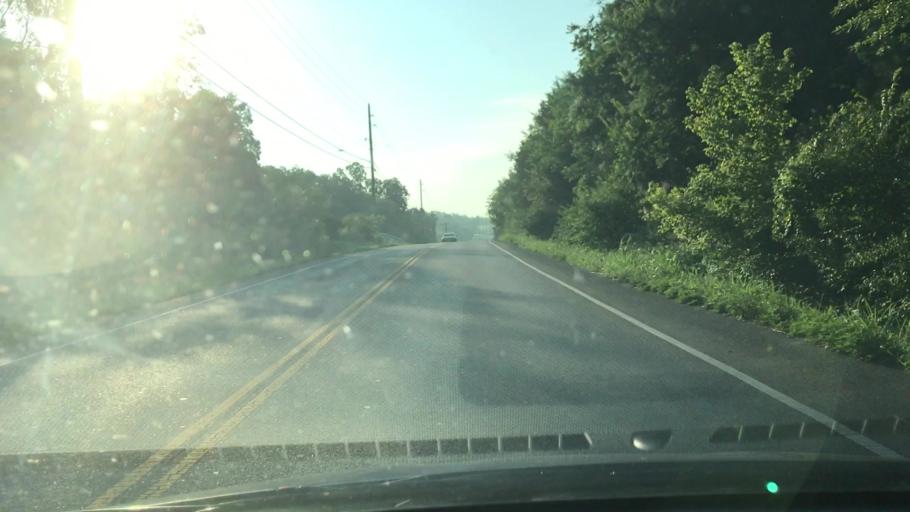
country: US
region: Tennessee
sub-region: Williamson County
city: Nolensville
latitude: 35.9913
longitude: -86.6794
